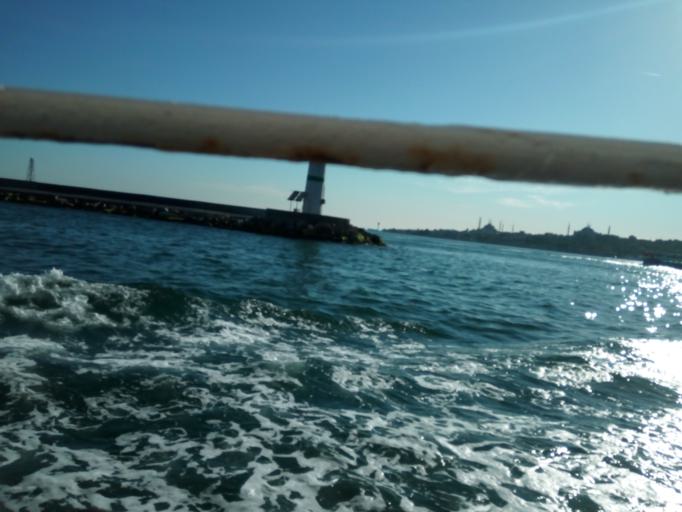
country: TR
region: Istanbul
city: UEskuedar
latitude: 41.0096
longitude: 29.0028
